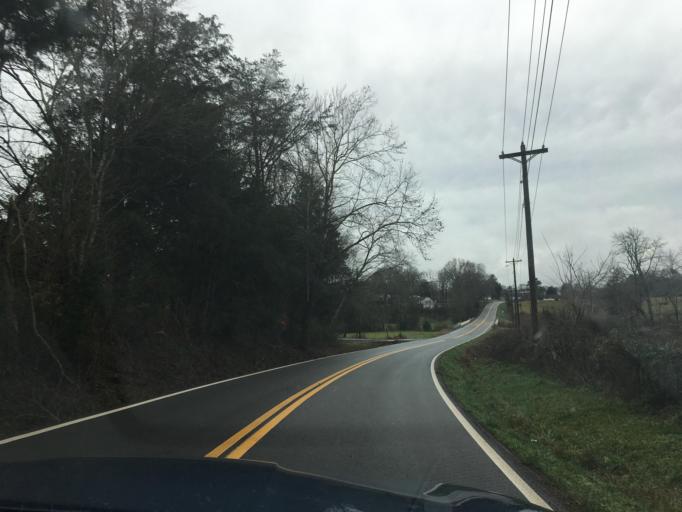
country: US
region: Tennessee
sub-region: McMinn County
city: Englewood
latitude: 35.4201
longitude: -84.4761
